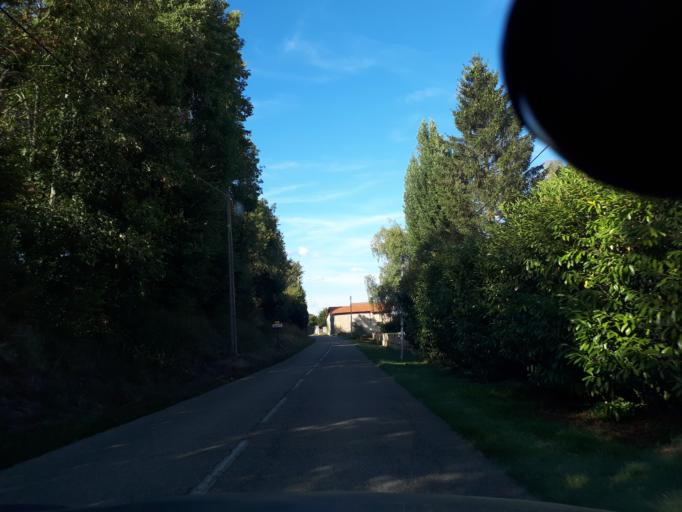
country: FR
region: Rhone-Alpes
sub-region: Departement de l'Isere
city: Maubec
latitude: 45.5267
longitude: 5.2544
